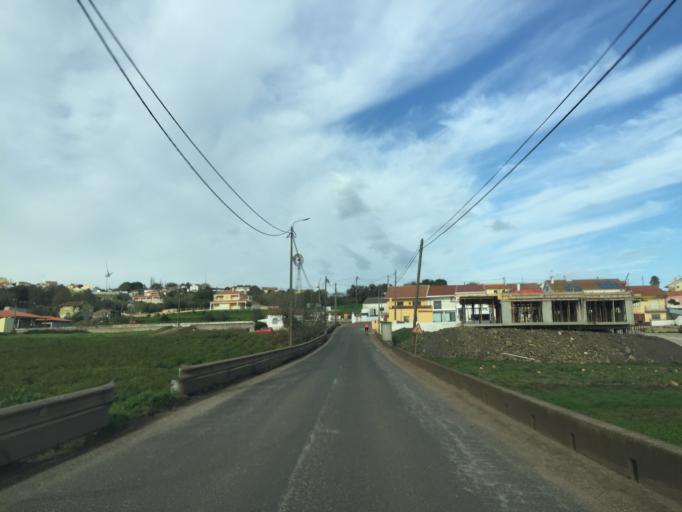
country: PT
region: Lisbon
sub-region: Sintra
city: Almargem
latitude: 38.8347
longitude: -9.2525
